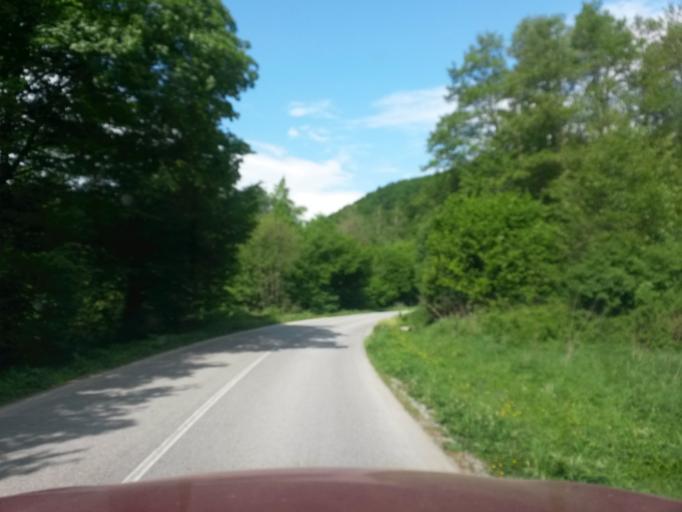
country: SK
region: Kosicky
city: Moldava nad Bodvou
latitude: 48.7257
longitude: 21.0775
